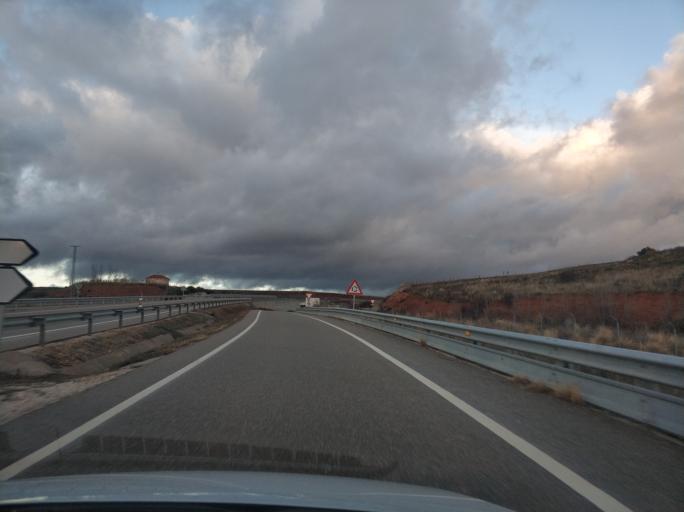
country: ES
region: Castille and Leon
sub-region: Provincia de Segovia
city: Ayllon
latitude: 41.4145
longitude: -3.4085
